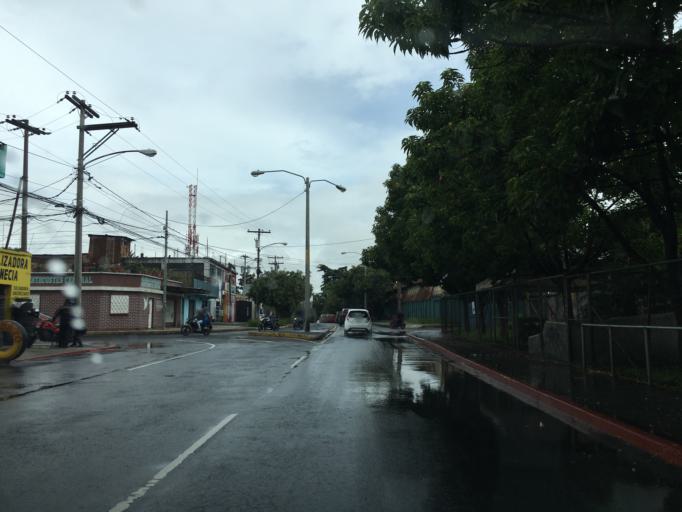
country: GT
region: Guatemala
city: Guatemala City
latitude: 14.6287
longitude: -90.5111
